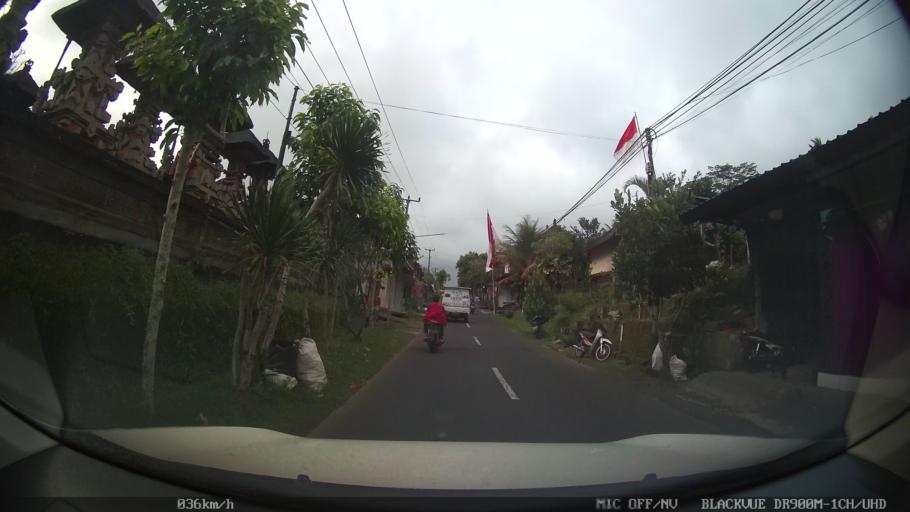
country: ID
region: Bali
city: Banjar Triwangsakeliki
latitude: -8.4515
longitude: 115.2617
